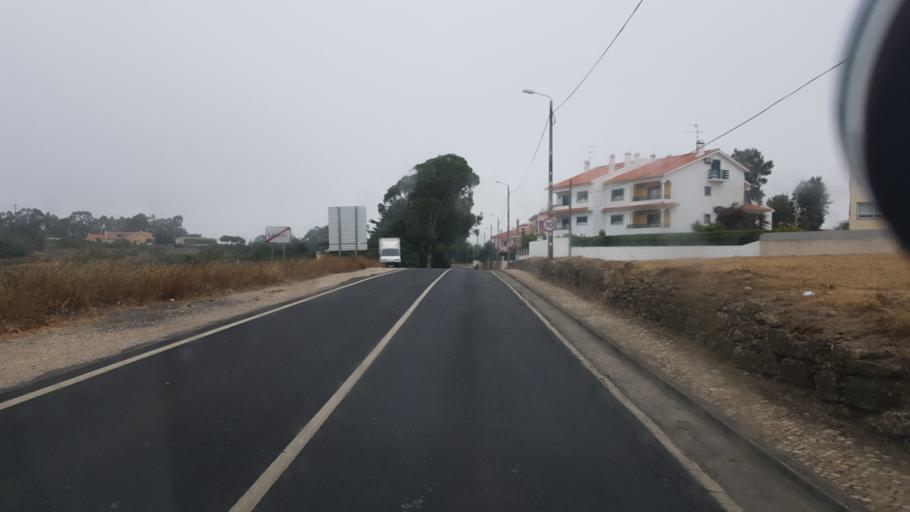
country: PT
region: Lisbon
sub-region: Sintra
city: Sintra
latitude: 38.8154
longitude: -9.3682
